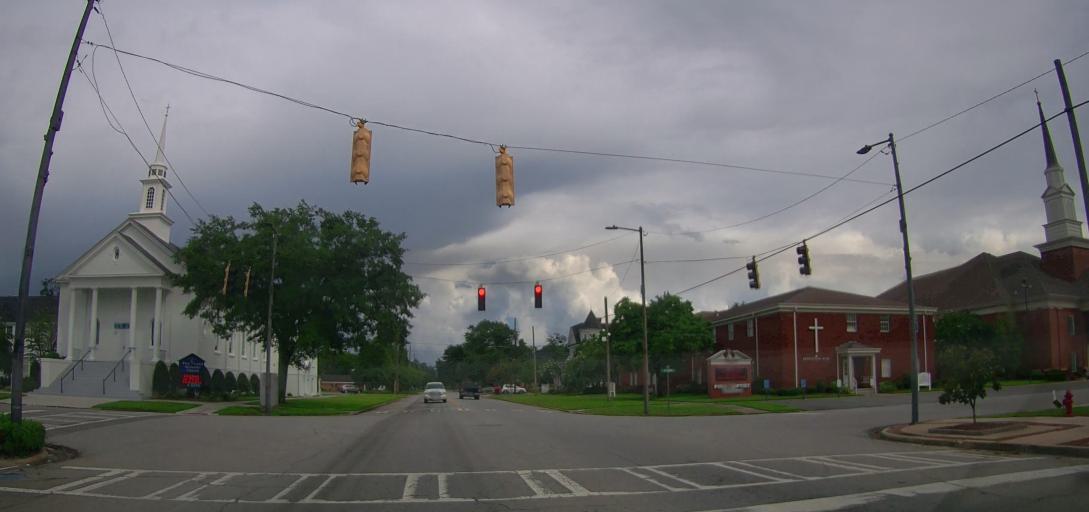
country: US
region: Georgia
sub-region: Wayne County
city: Jesup
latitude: 31.6038
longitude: -81.8813
